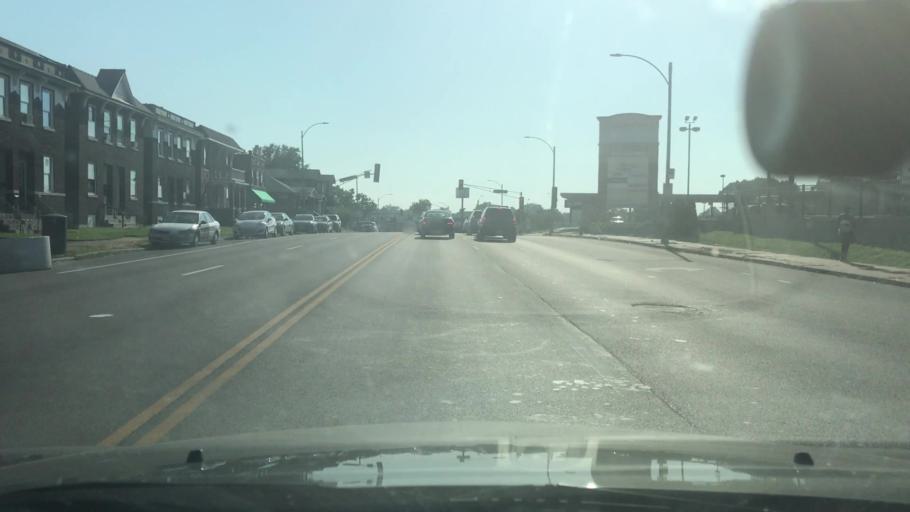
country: US
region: Missouri
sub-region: City of Saint Louis
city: St. Louis
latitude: 38.5917
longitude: -90.2492
